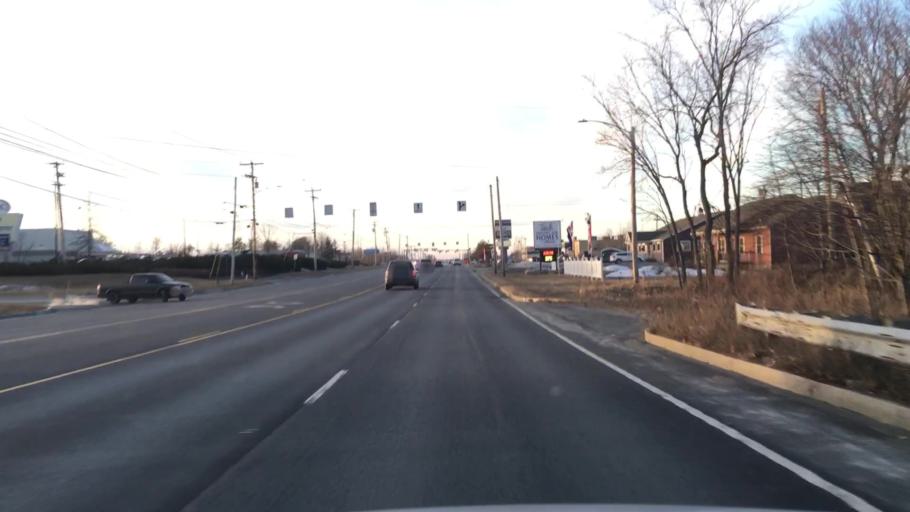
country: US
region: Maine
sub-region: Penobscot County
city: Brewer
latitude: 44.7749
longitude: -68.7297
